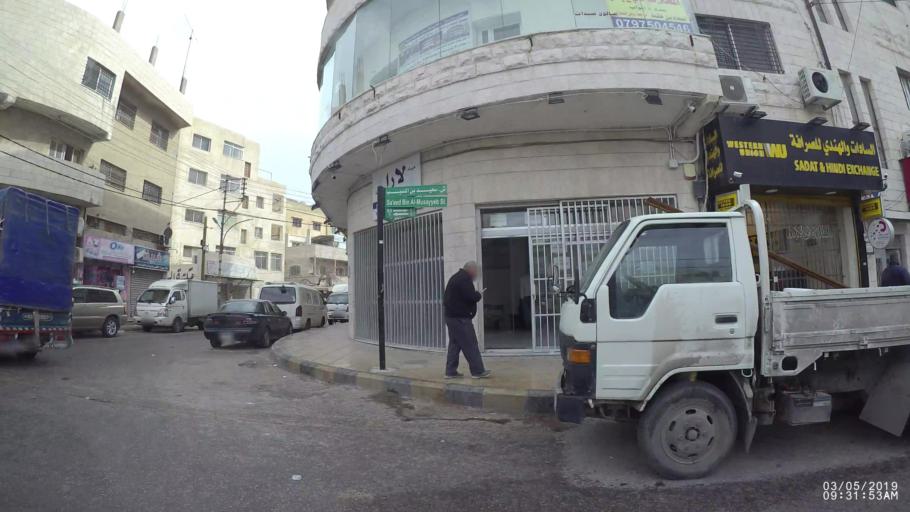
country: JO
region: Amman
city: Amman
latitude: 31.9765
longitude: 35.9248
